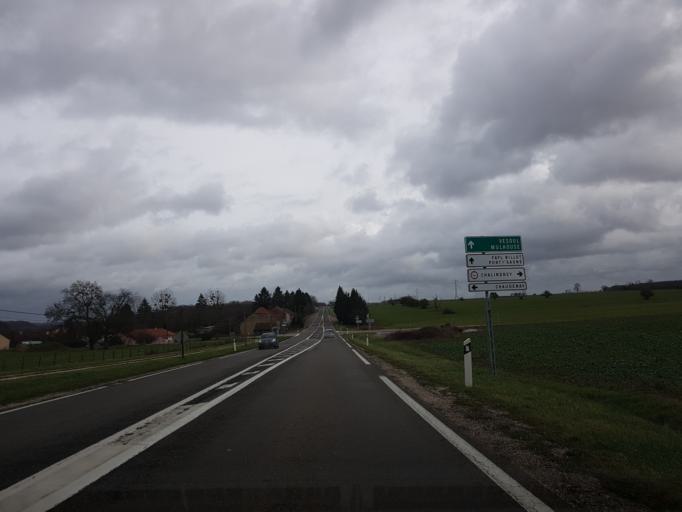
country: FR
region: Champagne-Ardenne
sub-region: Departement de la Haute-Marne
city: Chalindrey
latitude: 47.8179
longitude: 5.4892
